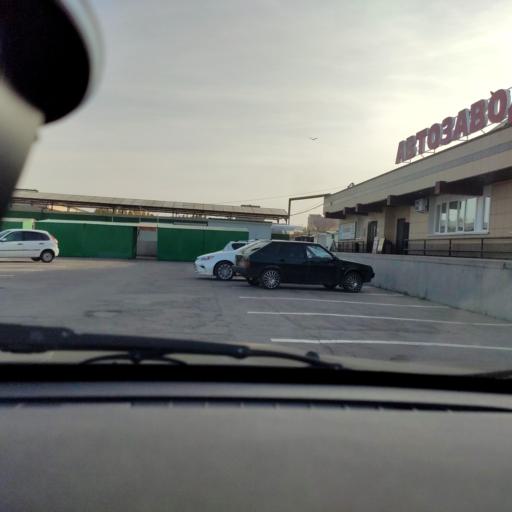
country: RU
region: Samara
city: Tol'yatti
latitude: 53.5415
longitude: 49.2827
